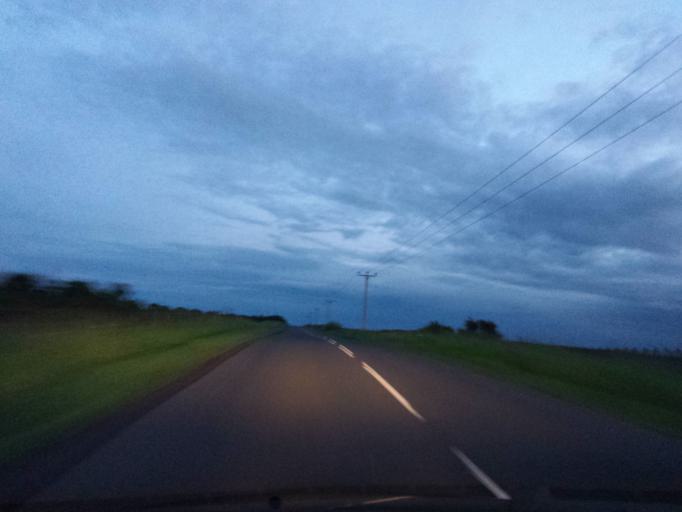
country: GB
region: Scotland
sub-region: The Scottish Borders
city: Duns
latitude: 55.7241
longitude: -2.4521
